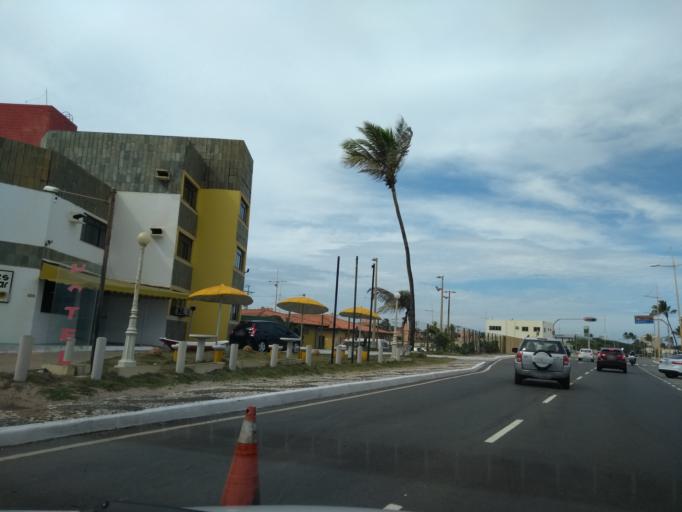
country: BR
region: Bahia
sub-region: Lauro De Freitas
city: Lauro de Freitas
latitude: -12.9646
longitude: -38.4025
